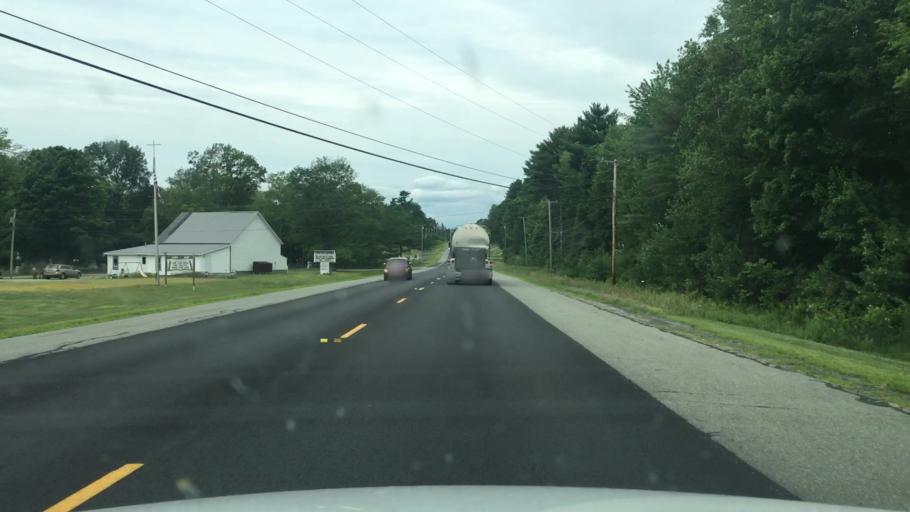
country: US
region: Maine
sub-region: Waldo County
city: Palermo
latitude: 44.3782
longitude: -69.4511
